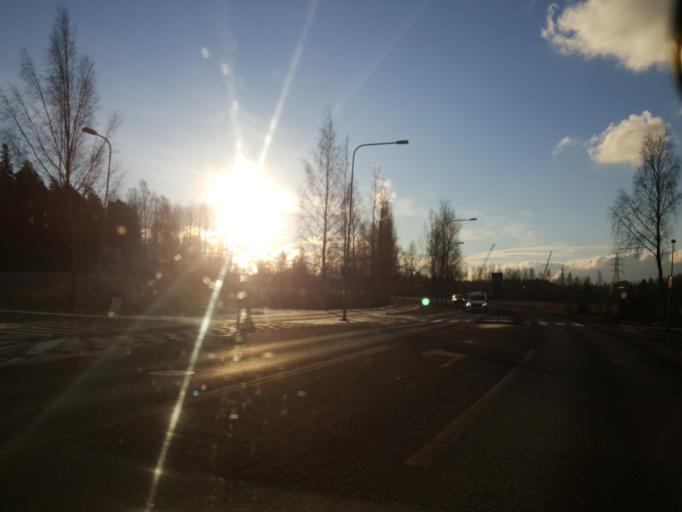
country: FI
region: Uusimaa
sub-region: Helsinki
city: Vantaa
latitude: 60.2472
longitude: 24.9765
